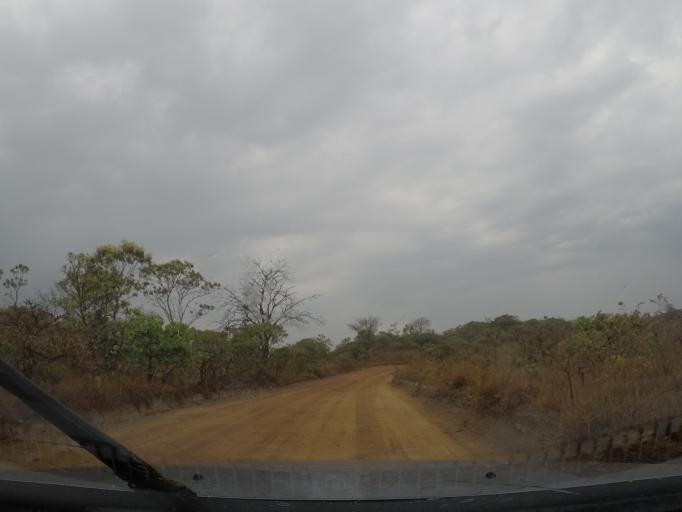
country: BR
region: Goias
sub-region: Pirenopolis
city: Pirenopolis
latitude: -15.8256
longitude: -48.9054
